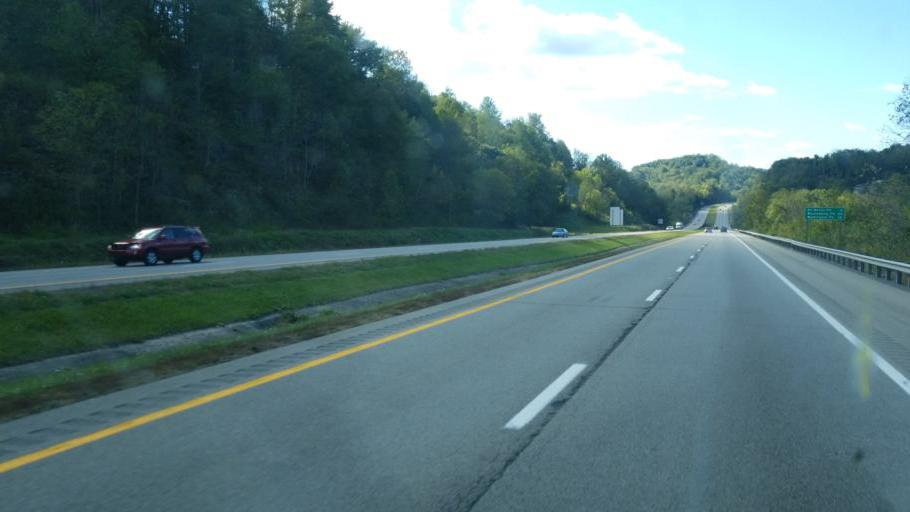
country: US
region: West Virginia
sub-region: Monongalia County
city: Star City
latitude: 39.6646
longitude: -80.0149
